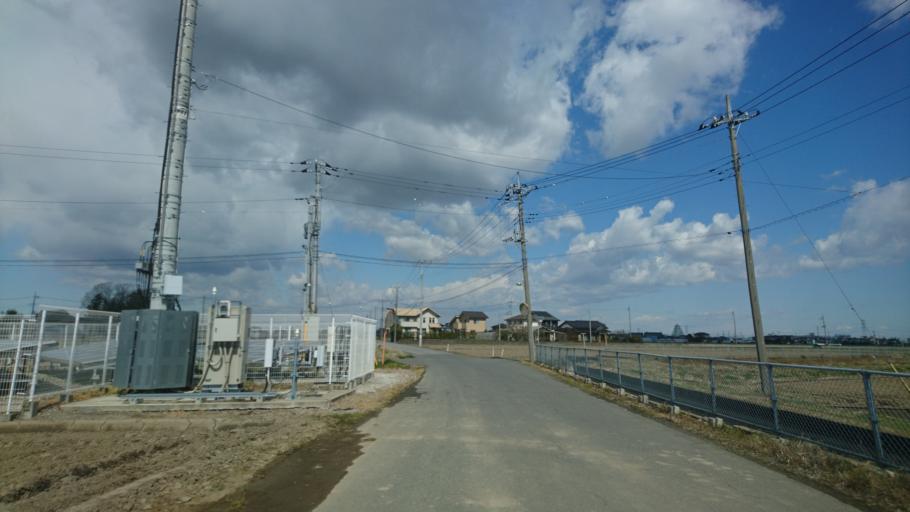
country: JP
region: Ibaraki
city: Ishige
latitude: 36.0975
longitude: 139.9805
